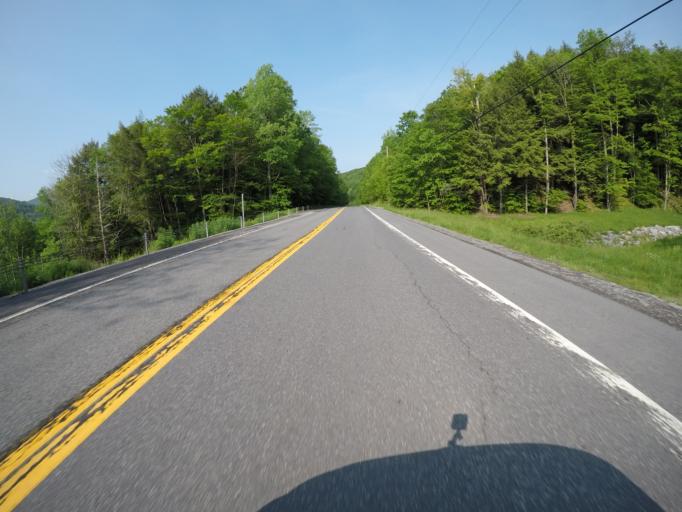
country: US
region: New York
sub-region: Delaware County
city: Delhi
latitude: 42.1273
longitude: -74.7158
